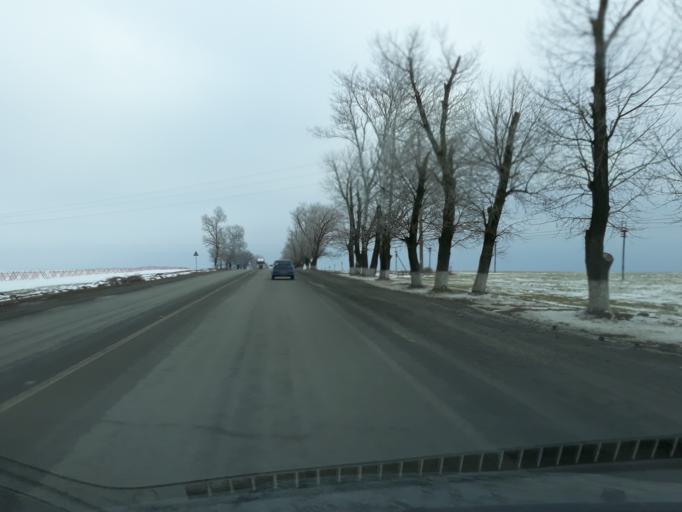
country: RU
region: Rostov
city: Primorka
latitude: 47.3209
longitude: 39.0879
